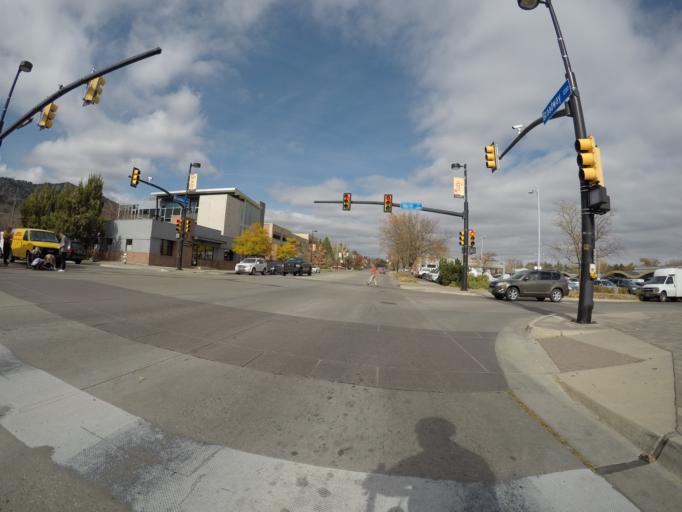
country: US
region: Colorado
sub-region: Boulder County
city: Boulder
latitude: 40.0244
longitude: -105.2820
